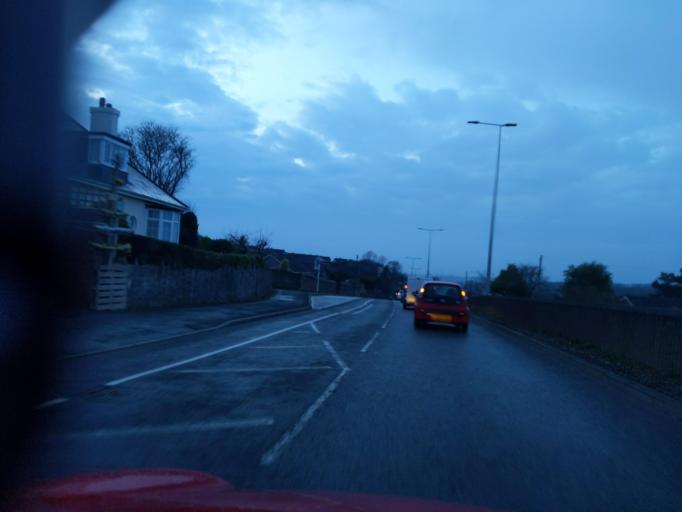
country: GB
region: England
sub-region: Plymouth
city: Plymstock
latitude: 50.3623
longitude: -4.0685
